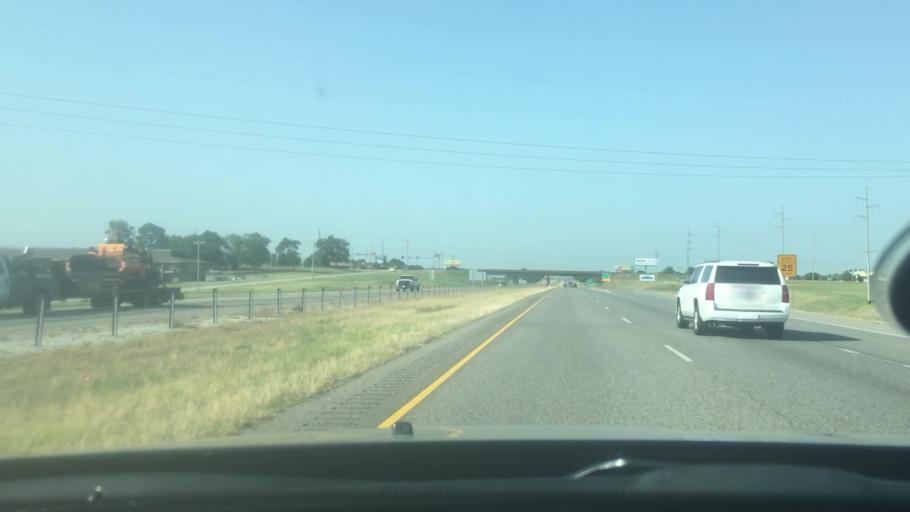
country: US
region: Oklahoma
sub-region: Bryan County
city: Durant
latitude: 34.0083
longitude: -96.3977
